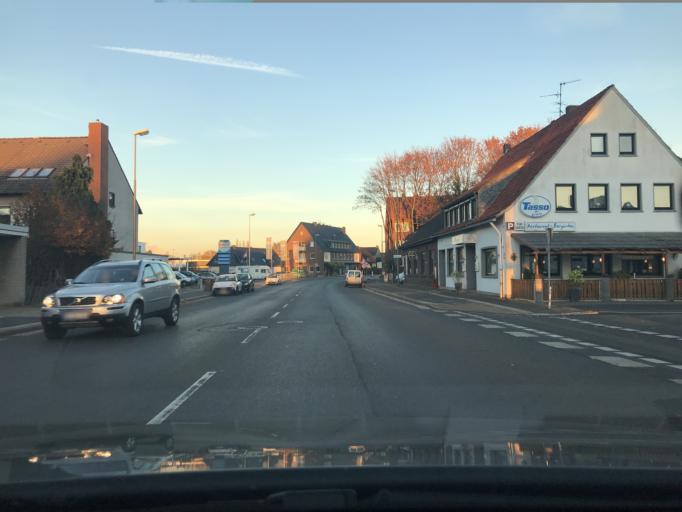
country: DE
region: North Rhine-Westphalia
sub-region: Regierungsbezirk Dusseldorf
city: Moers
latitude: 51.4505
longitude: 6.6066
